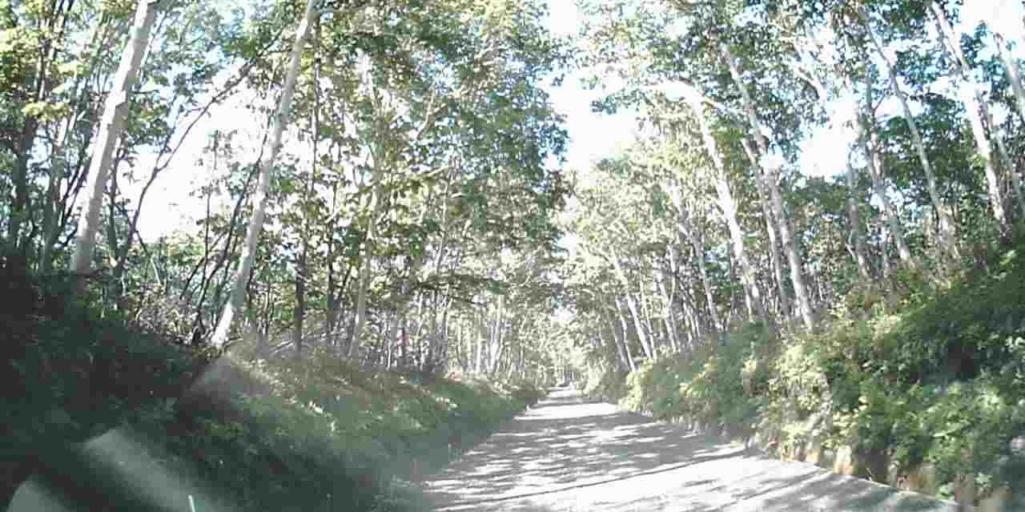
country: JP
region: Hokkaido
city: Shiraoi
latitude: 42.7031
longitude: 141.3933
